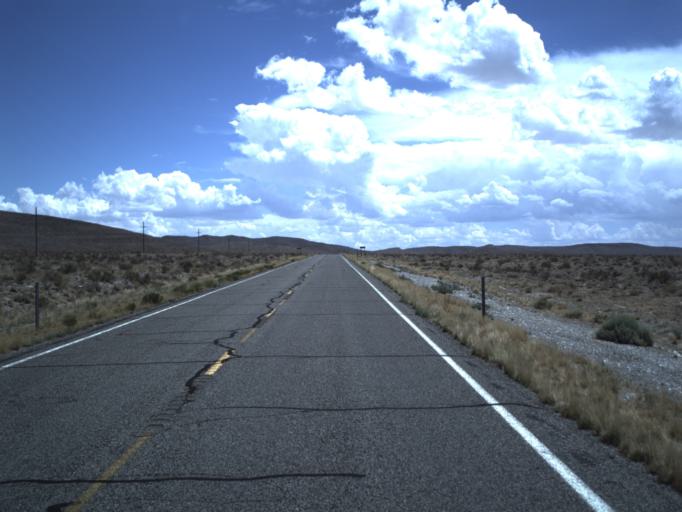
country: US
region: Utah
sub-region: Beaver County
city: Milford
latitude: 39.0303
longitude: -113.3815
